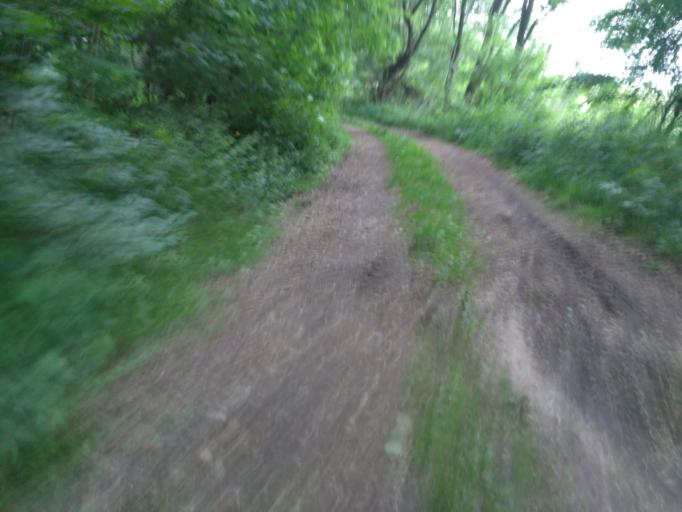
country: DE
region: Brandenburg
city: Elsterwerda
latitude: 51.4882
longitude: 13.5244
